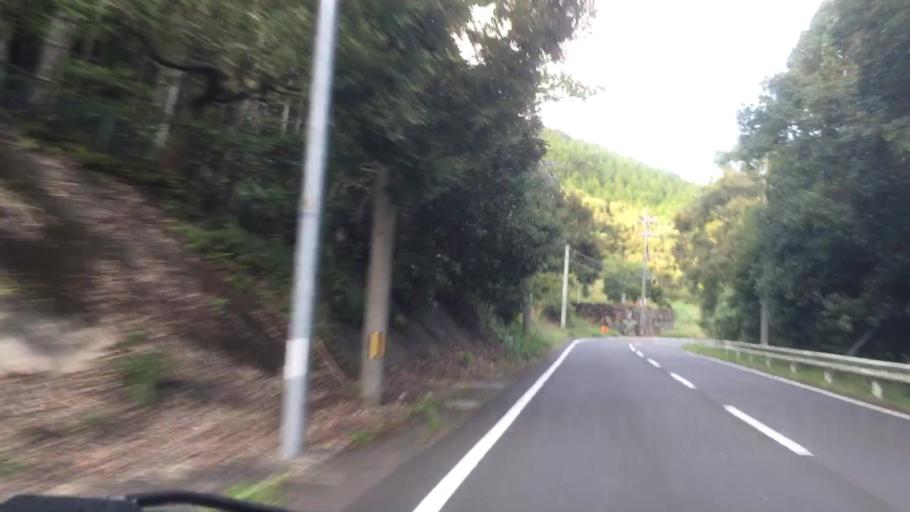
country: JP
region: Nagasaki
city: Sasebo
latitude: 32.9659
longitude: 129.6888
